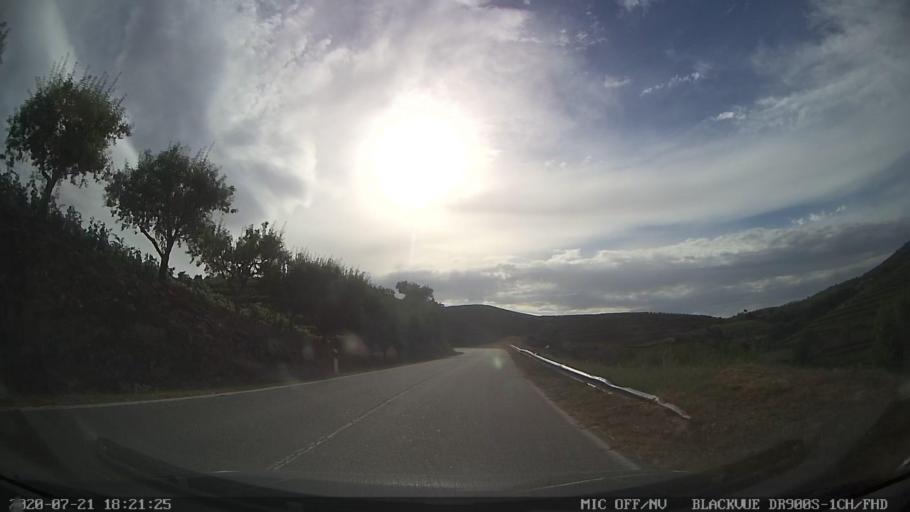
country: PT
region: Viseu
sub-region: Sao Joao da Pesqueira
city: Sao Joao da Pesqueira
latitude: 41.0831
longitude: -7.3878
